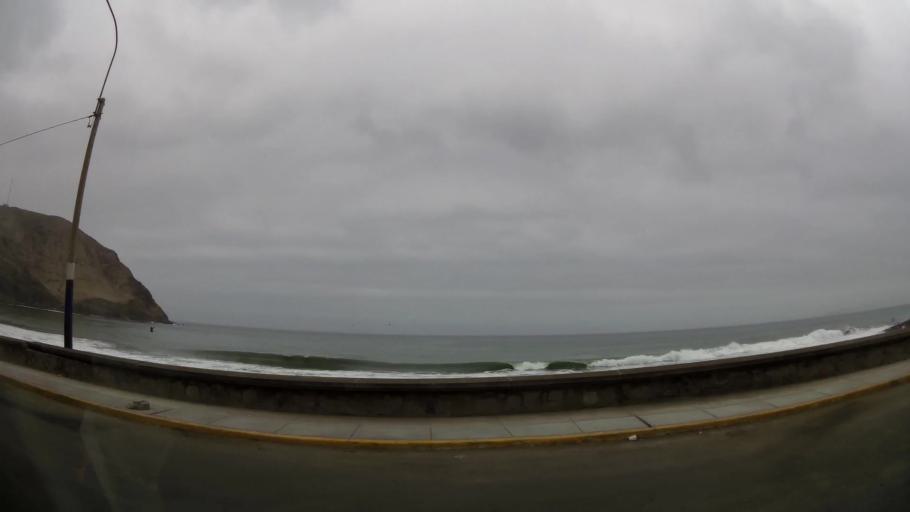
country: PE
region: Lima
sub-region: Lima
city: Surco
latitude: -12.1721
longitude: -77.0348
